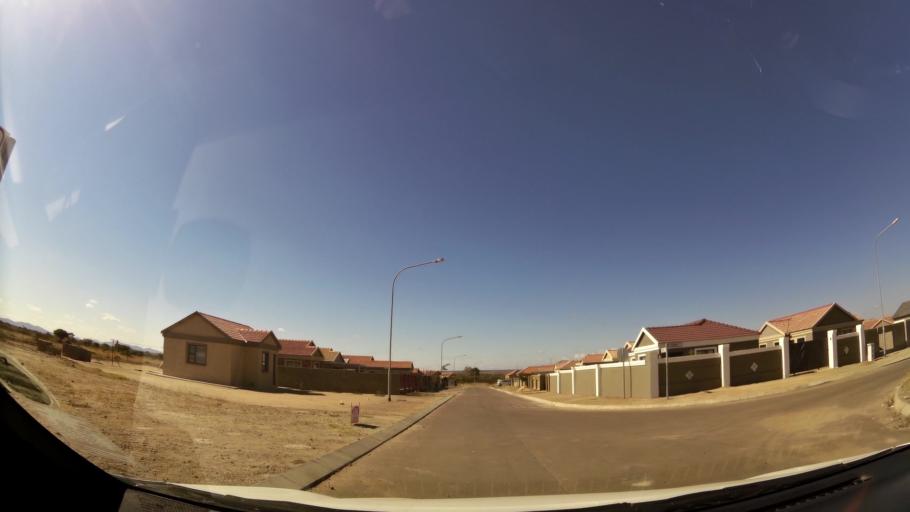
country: ZA
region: Limpopo
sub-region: Capricorn District Municipality
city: Polokwane
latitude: -23.8576
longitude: 29.4246
